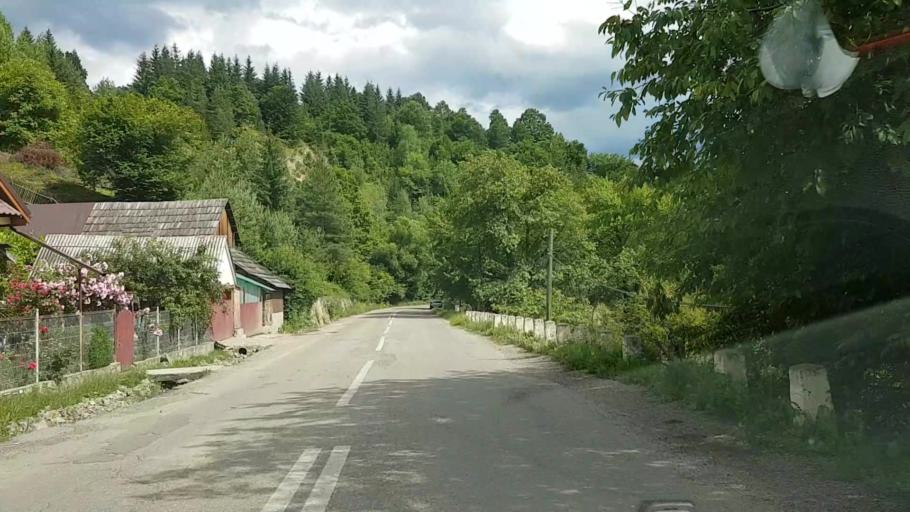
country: RO
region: Neamt
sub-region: Comuna Hangu
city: Hangu
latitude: 47.0290
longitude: 26.0666
